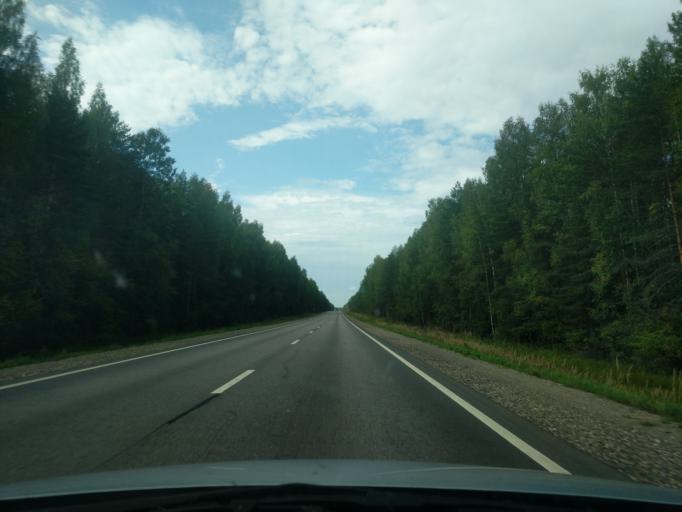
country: RU
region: Kostroma
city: Kadyy
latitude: 57.7963
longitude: 42.9179
